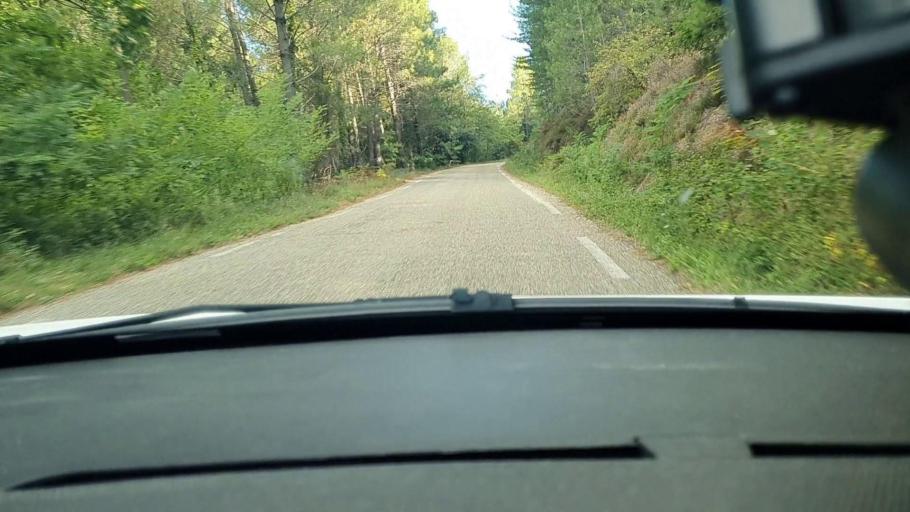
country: FR
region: Languedoc-Roussillon
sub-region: Departement du Gard
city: Branoux-les-Taillades
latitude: 44.3441
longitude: 3.9804
